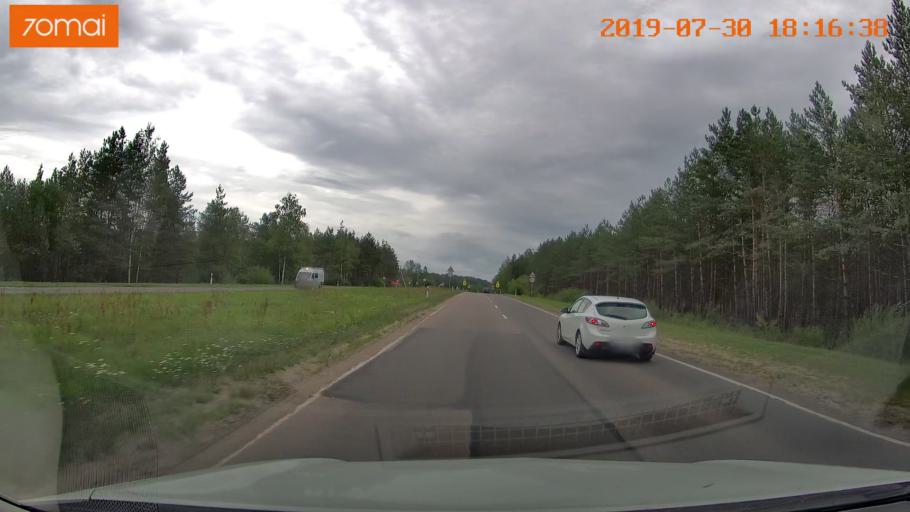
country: LT
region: Vilnius County
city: Rasos
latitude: 54.6923
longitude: 25.3754
